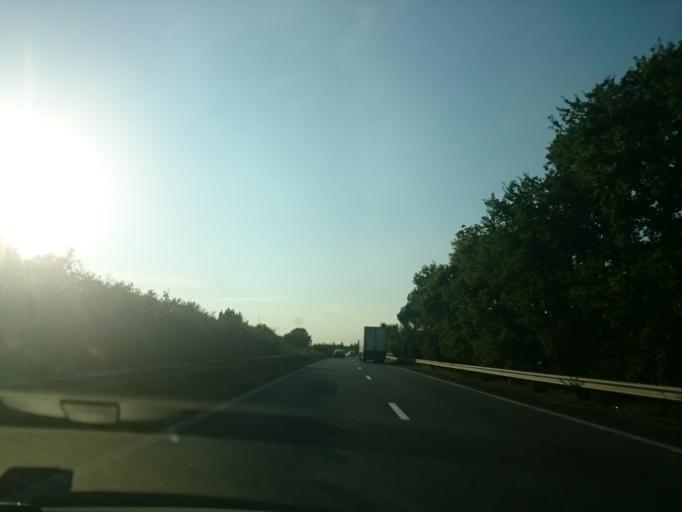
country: FR
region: Pays de la Loire
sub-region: Departement de la Loire-Atlantique
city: Missillac
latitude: 47.4839
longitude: -2.1979
